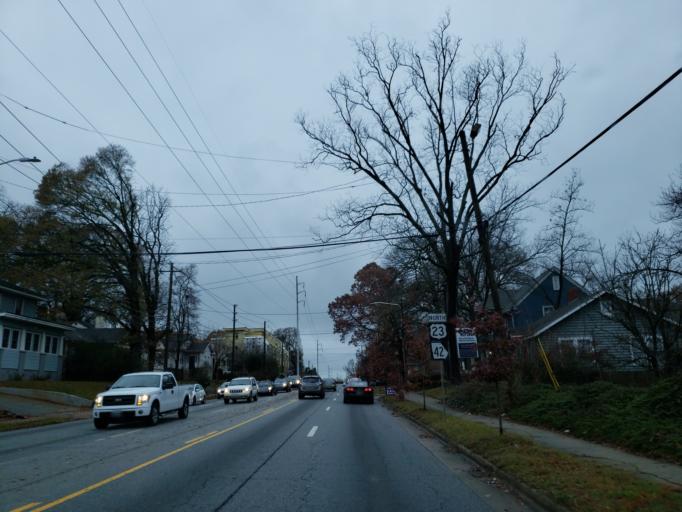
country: US
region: Georgia
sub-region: DeKalb County
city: Druid Hills
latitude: 33.7484
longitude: -84.3492
